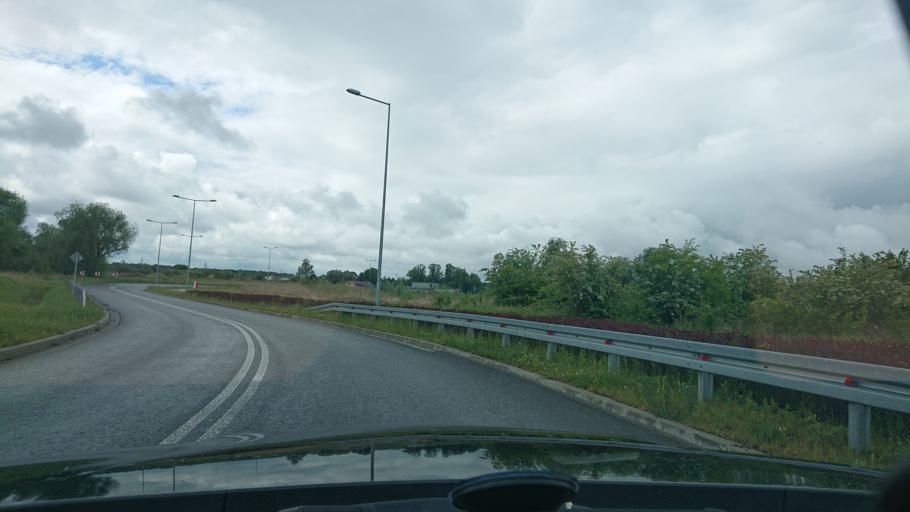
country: PL
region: Greater Poland Voivodeship
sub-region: Powiat gnieznienski
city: Gniezno
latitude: 52.5251
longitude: 17.6235
